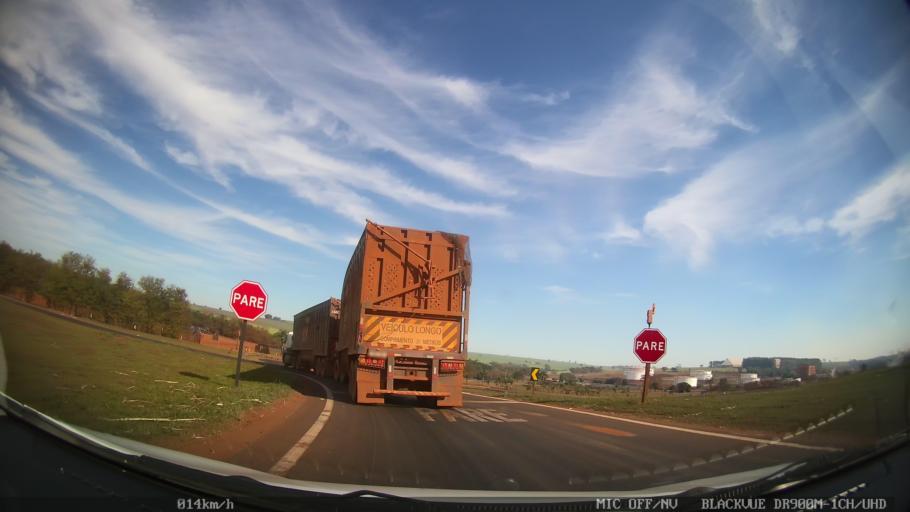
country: BR
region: Sao Paulo
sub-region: Americo Brasiliense
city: Americo Brasiliense
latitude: -21.7536
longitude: -48.0720
